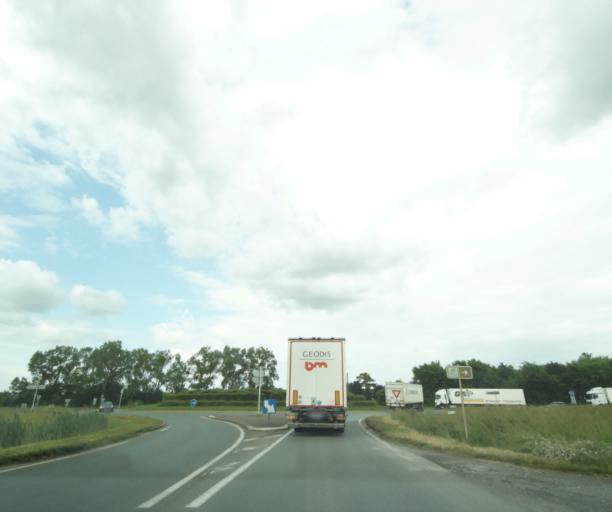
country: FR
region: Pays de la Loire
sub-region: Departement de Maine-et-Loire
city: Vivy
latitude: 47.3080
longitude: -0.0314
